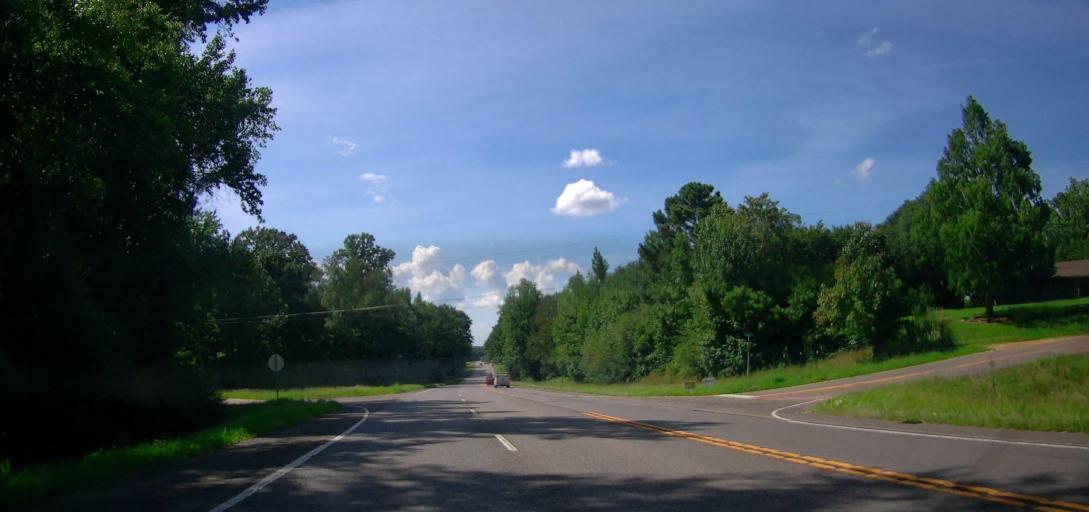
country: US
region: Alabama
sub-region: Pickens County
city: Gordo
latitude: 33.2915
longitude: -87.8716
